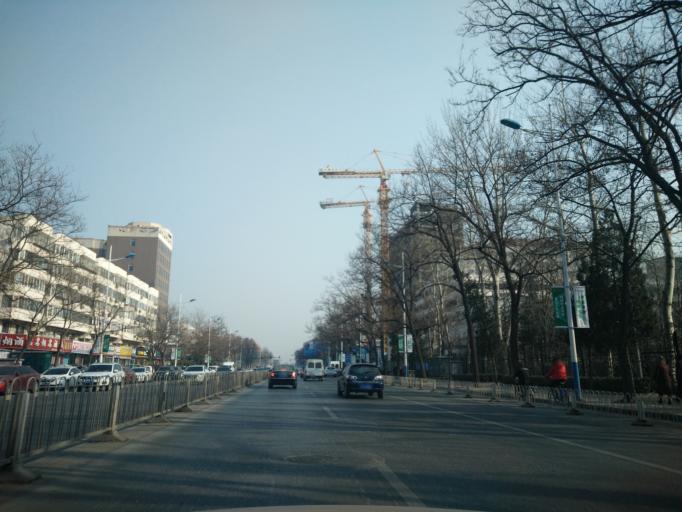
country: CN
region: Beijing
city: Daxing
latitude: 39.7413
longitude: 116.3302
